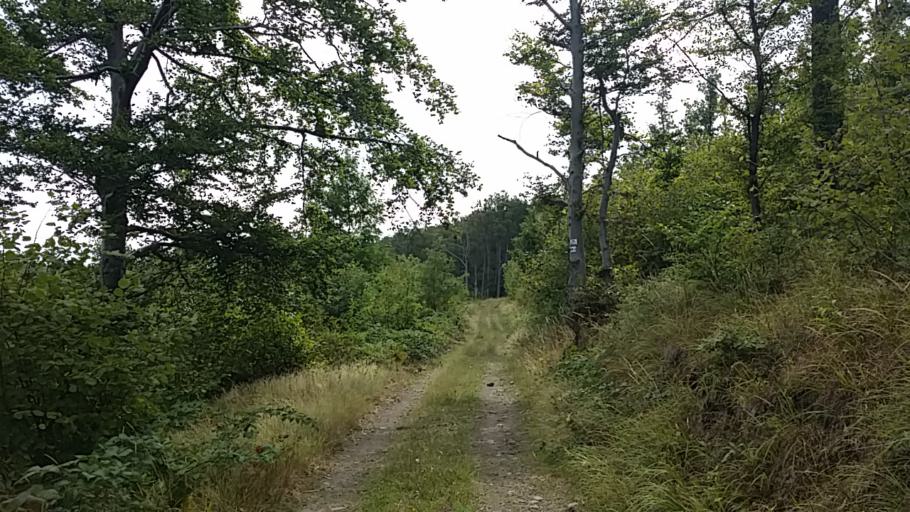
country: HU
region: Pest
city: Pilisszentkereszt
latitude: 47.6981
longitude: 18.9244
